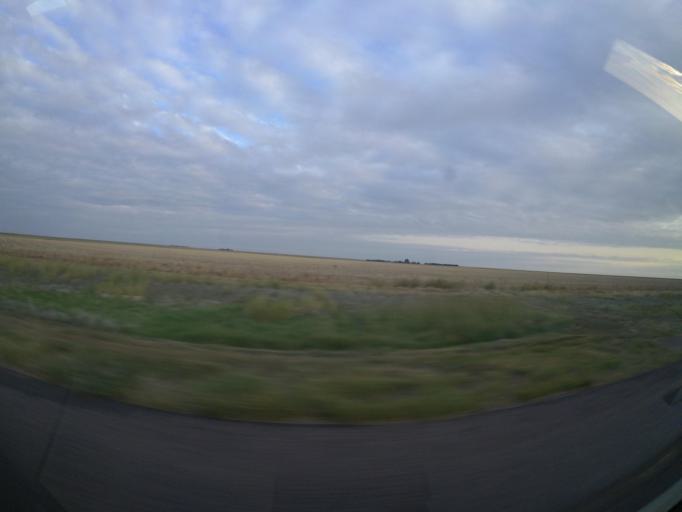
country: US
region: Kansas
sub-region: Cheyenne County
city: Saint Francis
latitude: 39.7496
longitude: -102.0538
